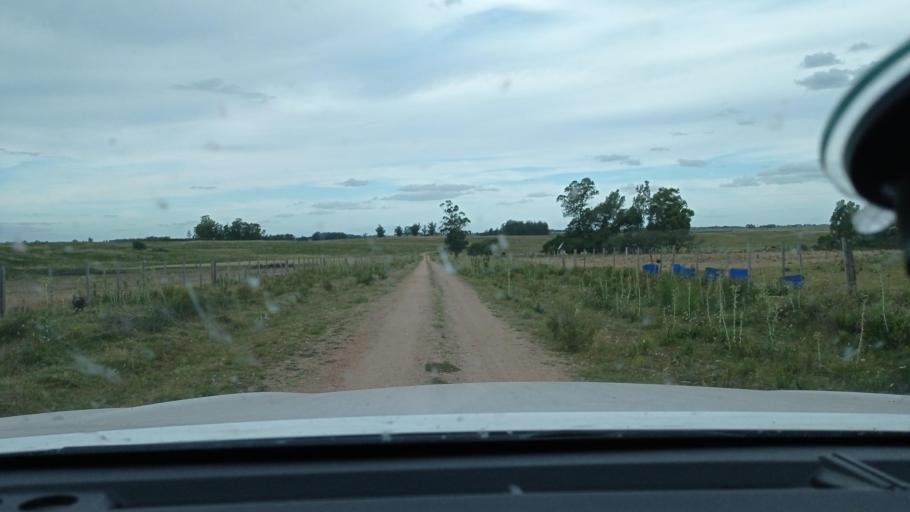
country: UY
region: Florida
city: Casupa
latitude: -34.1243
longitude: -55.8086
